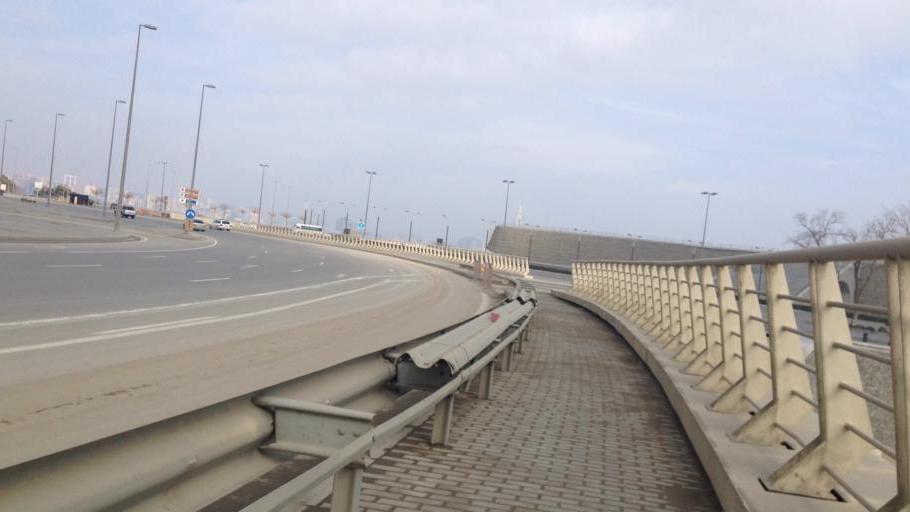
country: AZ
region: Baki
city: Badamdar
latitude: 40.3426
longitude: 49.8428
